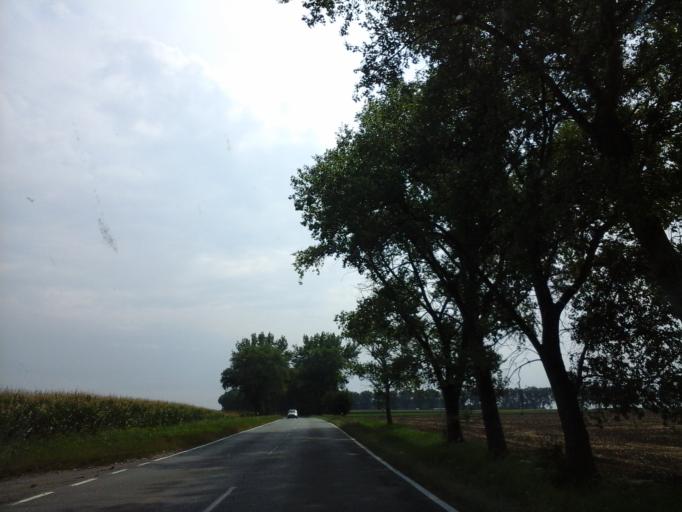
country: PL
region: Lower Silesian Voivodeship
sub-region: Powiat strzelinski
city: Strzelin
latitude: 50.8812
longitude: 17.0622
